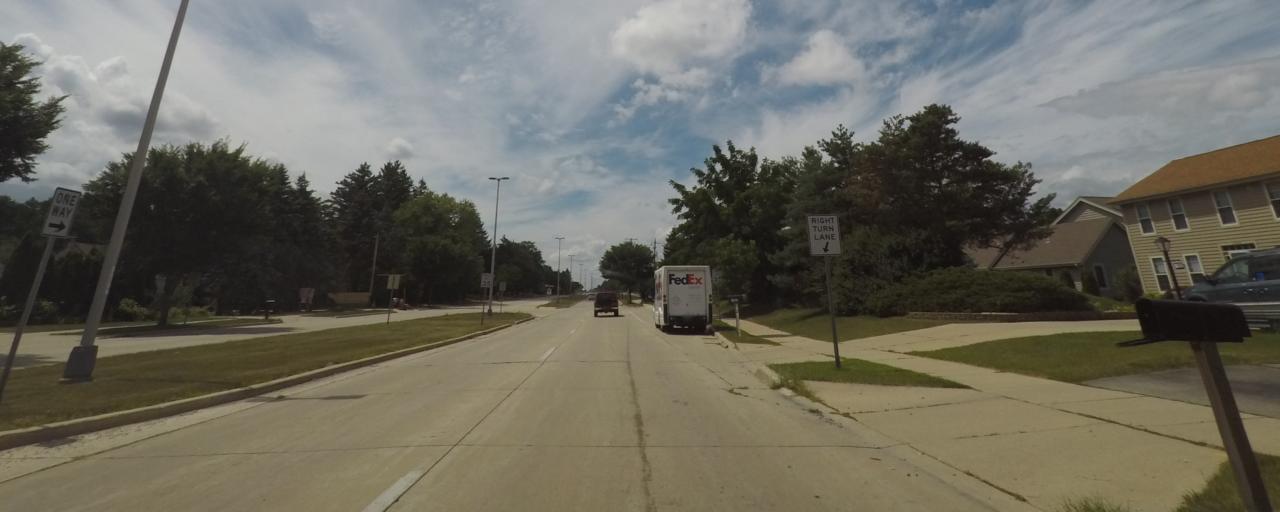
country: US
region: Wisconsin
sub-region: Milwaukee County
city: Hales Corners
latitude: 42.9592
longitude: -88.0611
